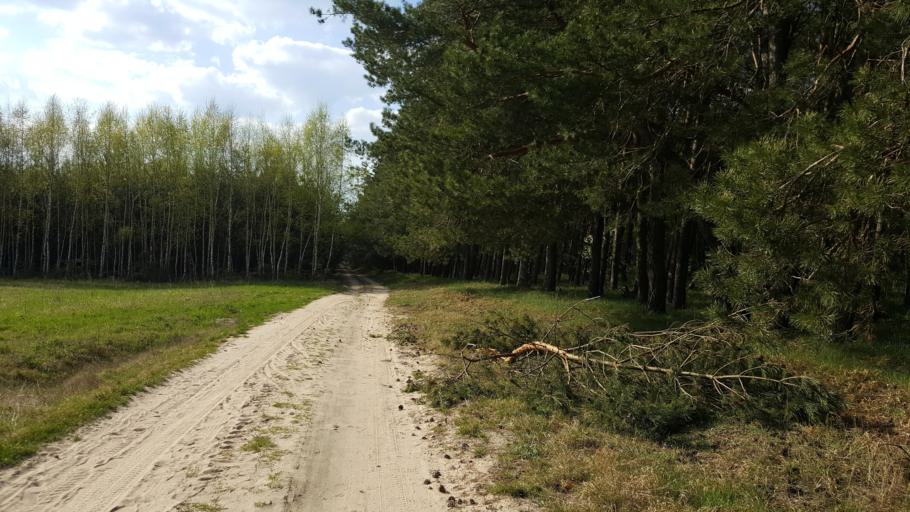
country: BY
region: Brest
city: Kamyanyets
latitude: 52.3816
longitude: 23.8358
